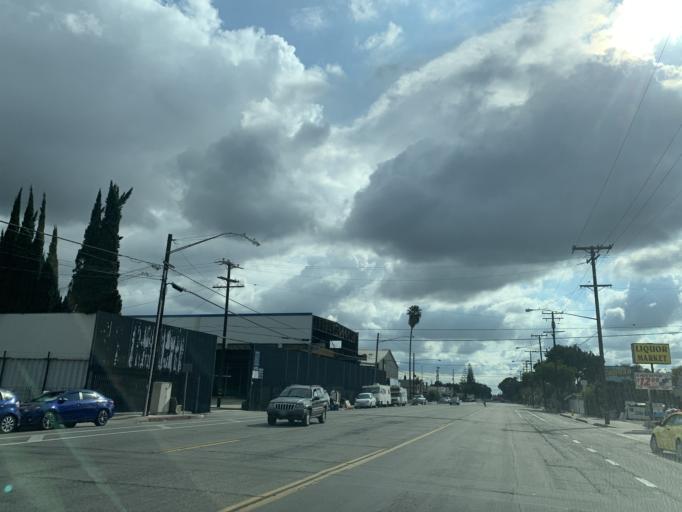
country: US
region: California
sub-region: Los Angeles County
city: Florence-Graham
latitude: 33.9816
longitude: -118.2413
